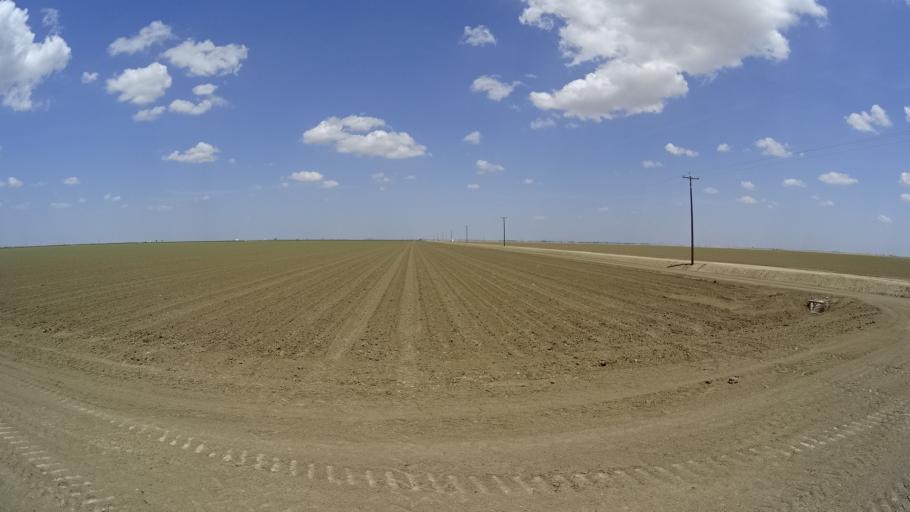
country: US
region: California
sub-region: Kings County
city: Lemoore Station
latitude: 36.1894
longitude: -119.9236
